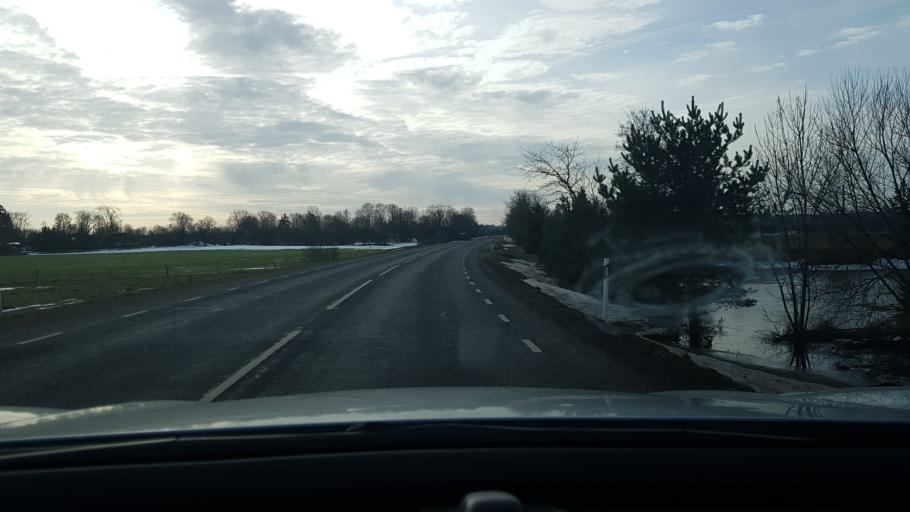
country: EE
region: Saare
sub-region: Kuressaare linn
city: Kuressaare
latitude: 58.2949
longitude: 22.5422
